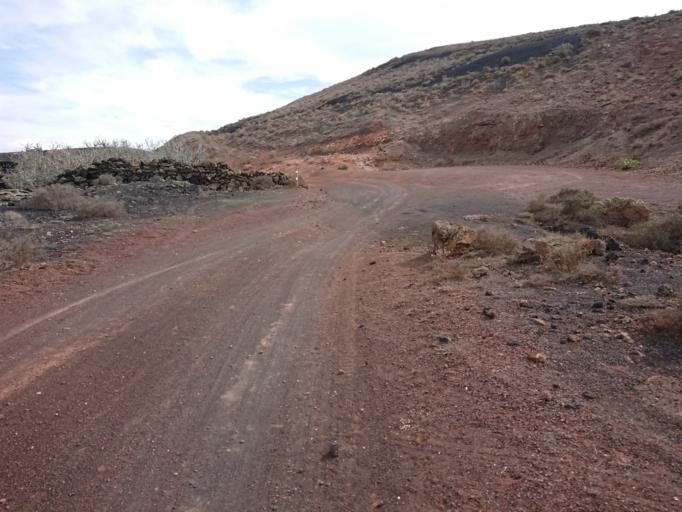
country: ES
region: Canary Islands
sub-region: Provincia de Las Palmas
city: Tinajo
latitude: 29.0208
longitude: -13.6782
